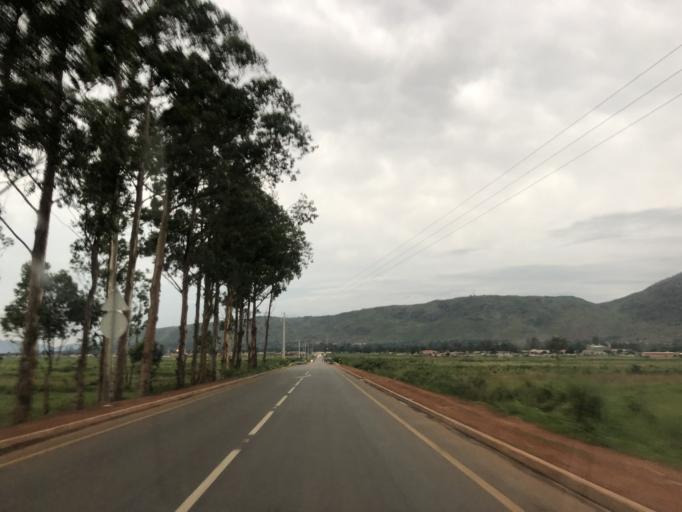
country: AO
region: Cuanza Sul
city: Uacu Cungo
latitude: -11.3377
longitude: 15.1031
